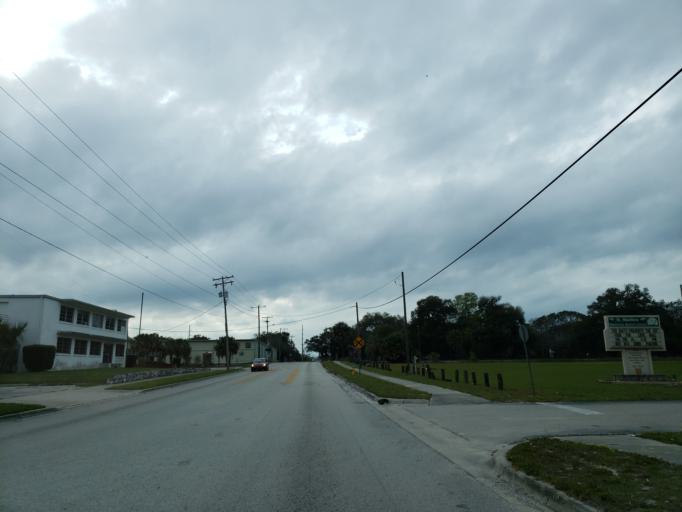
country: US
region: Florida
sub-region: Hillsborough County
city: East Lake-Orient Park
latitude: 27.9778
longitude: -82.4170
